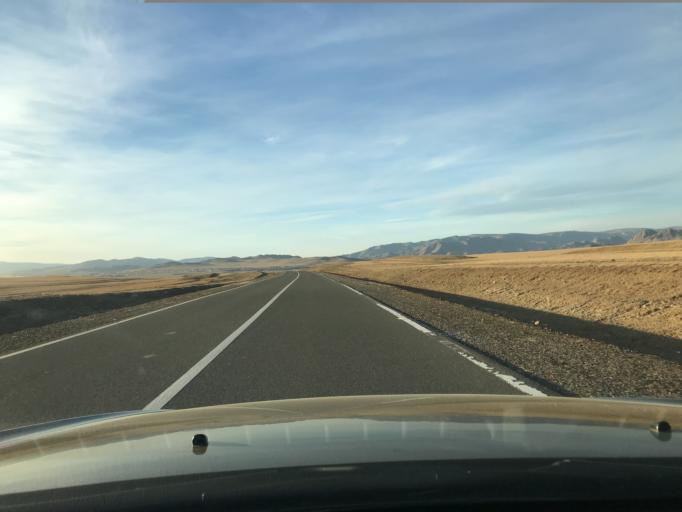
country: MN
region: Central Aimak
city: Arhust
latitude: 47.7595
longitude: 107.4417
